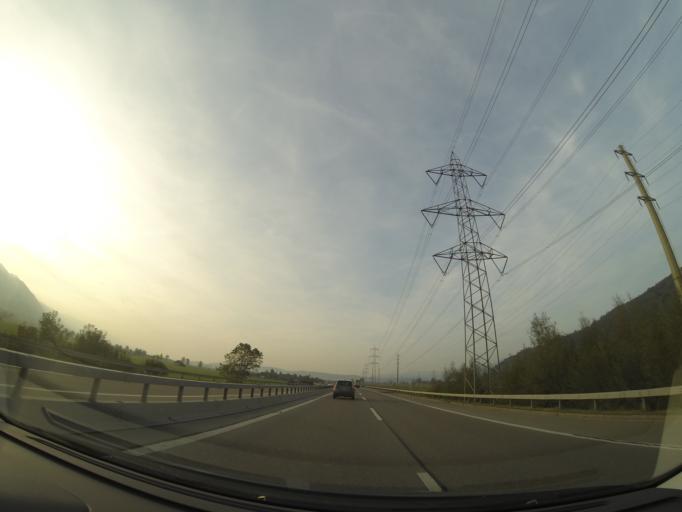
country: CH
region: Schwyz
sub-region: Bezirk March
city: Reichenburg
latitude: 47.1744
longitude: 9.0038
